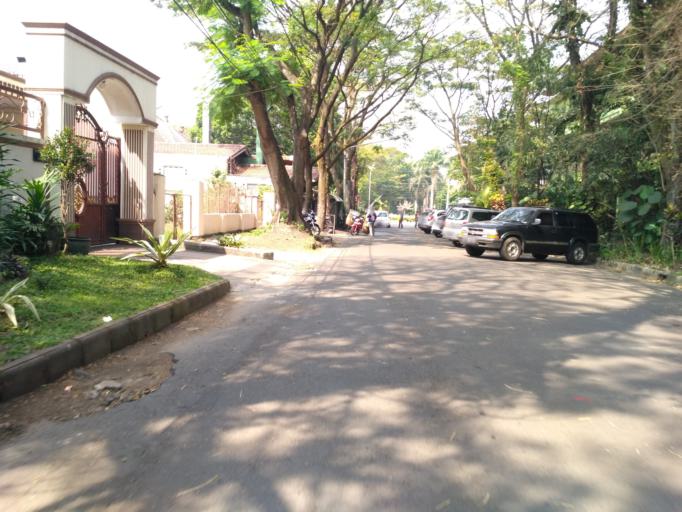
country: ID
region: East Java
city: Malang
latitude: -7.9765
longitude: 112.6356
